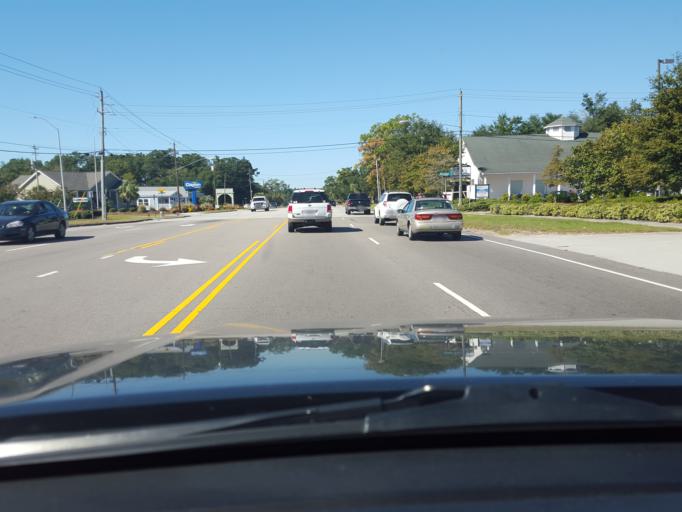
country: US
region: North Carolina
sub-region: New Hanover County
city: Seagate
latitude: 34.2080
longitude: -77.8646
